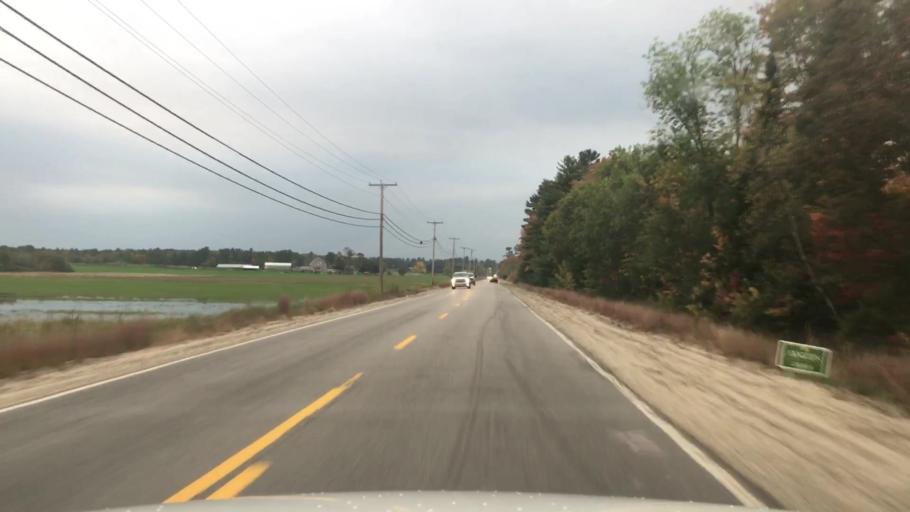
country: US
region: Maine
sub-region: York County
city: Buxton
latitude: 43.6401
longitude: -70.5240
